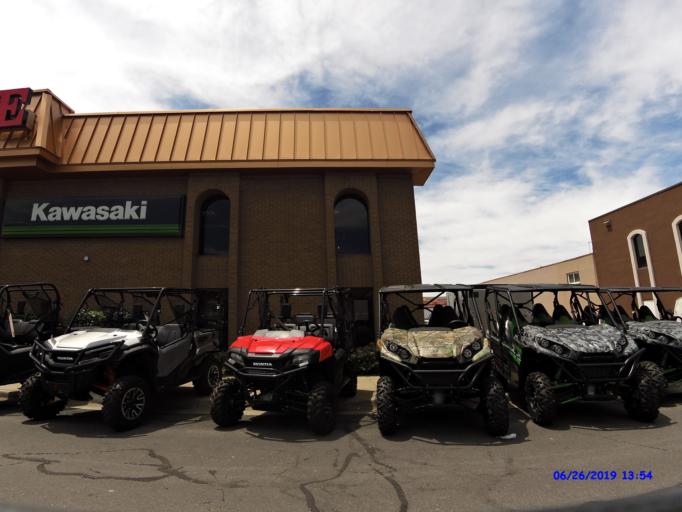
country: US
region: Utah
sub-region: Weber County
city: South Ogden
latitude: 41.1952
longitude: -111.9839
